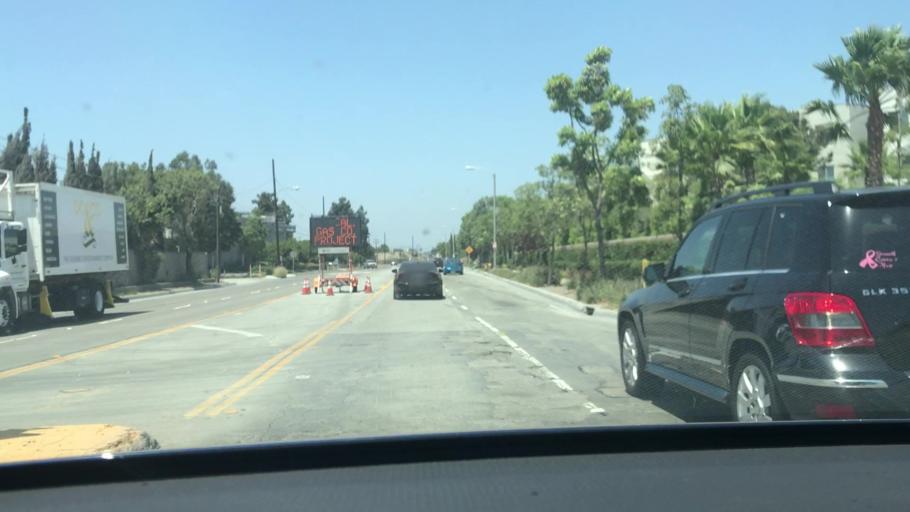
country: US
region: California
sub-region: Los Angeles County
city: Del Aire
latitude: 33.9121
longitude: -118.3787
